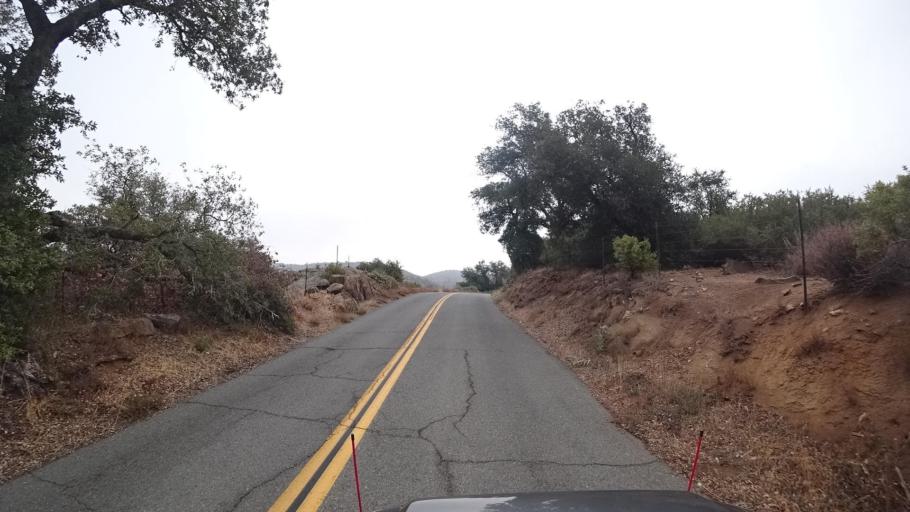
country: US
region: California
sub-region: San Diego County
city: Julian
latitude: 33.0608
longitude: -116.6073
